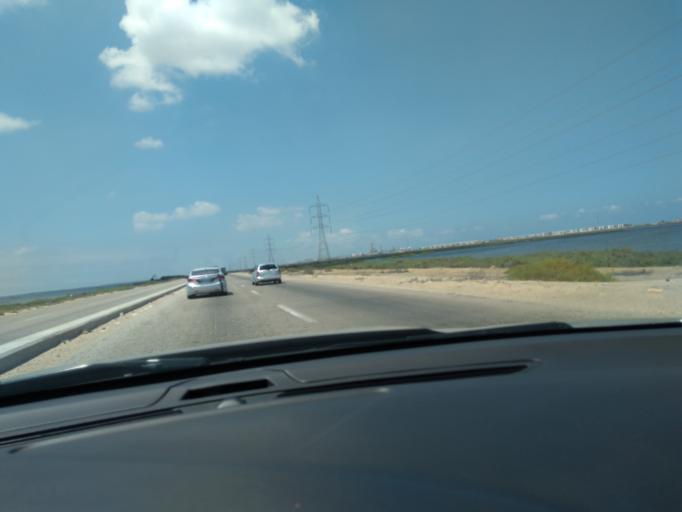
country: EG
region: Muhafazat Bur Sa`id
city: Port Said
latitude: 31.2792
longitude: 32.1934
